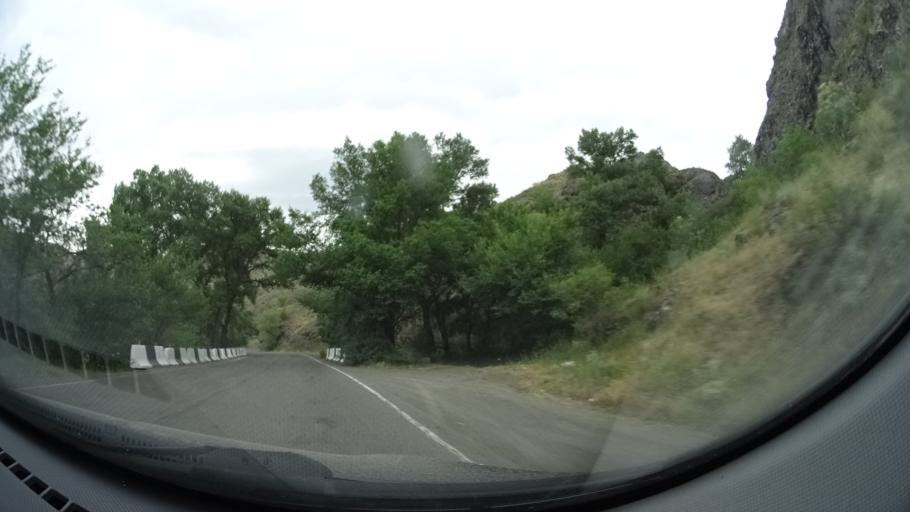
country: GE
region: Samtskhe-Javakheti
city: Akhaltsikhe
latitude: 41.6216
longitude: 43.0689
